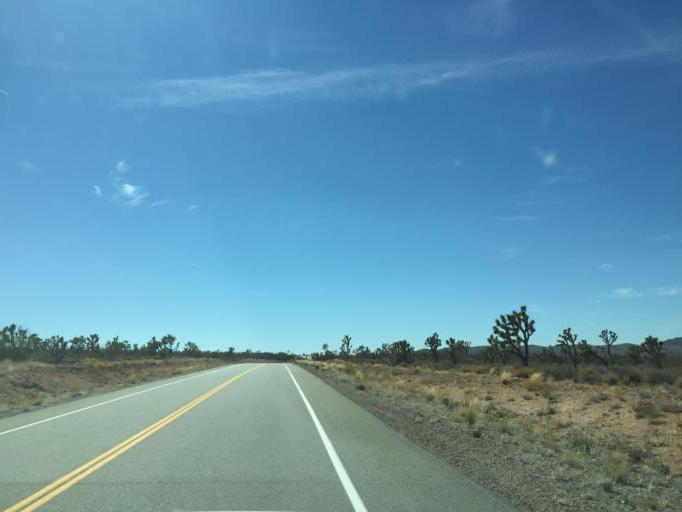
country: US
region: Arizona
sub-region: Mohave County
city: Meadview
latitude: 35.8857
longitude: -114.0438
